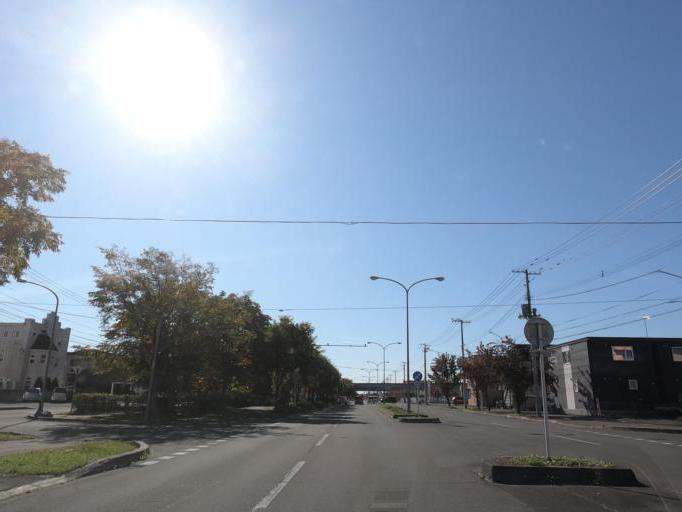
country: JP
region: Hokkaido
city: Obihiro
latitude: 42.9164
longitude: 143.2128
